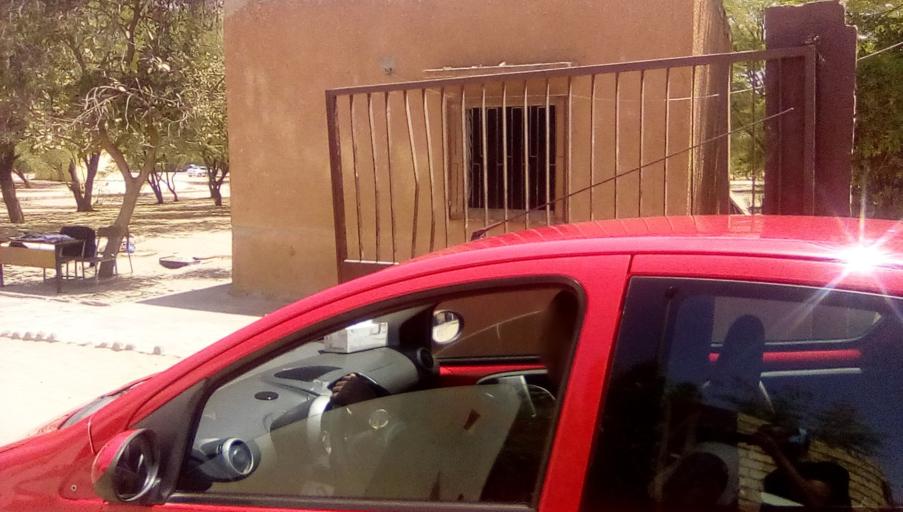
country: SN
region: Saint-Louis
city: Saint-Louis
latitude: 16.0604
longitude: -16.4217
